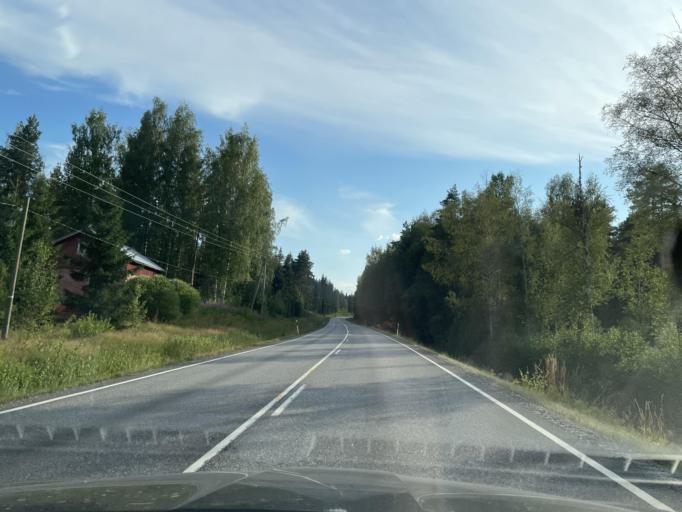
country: FI
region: Paijanne Tavastia
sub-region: Lahti
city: Padasjoki
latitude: 61.3347
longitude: 25.2198
